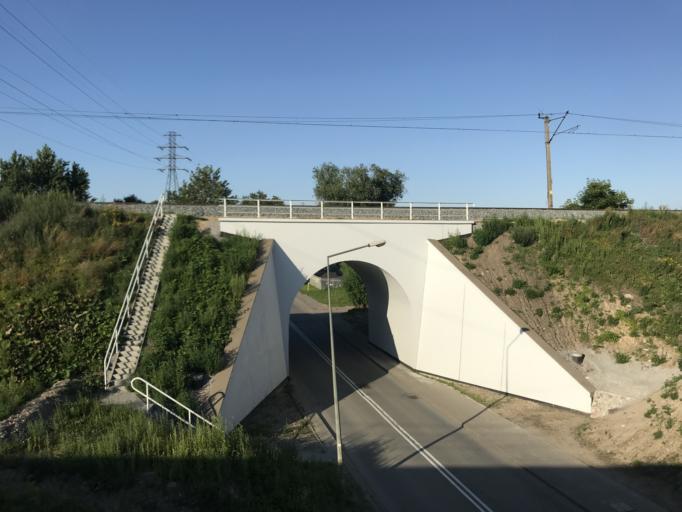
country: PL
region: Pomeranian Voivodeship
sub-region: Powiat tczewski
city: Tczew
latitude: 54.1083
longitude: 18.7798
